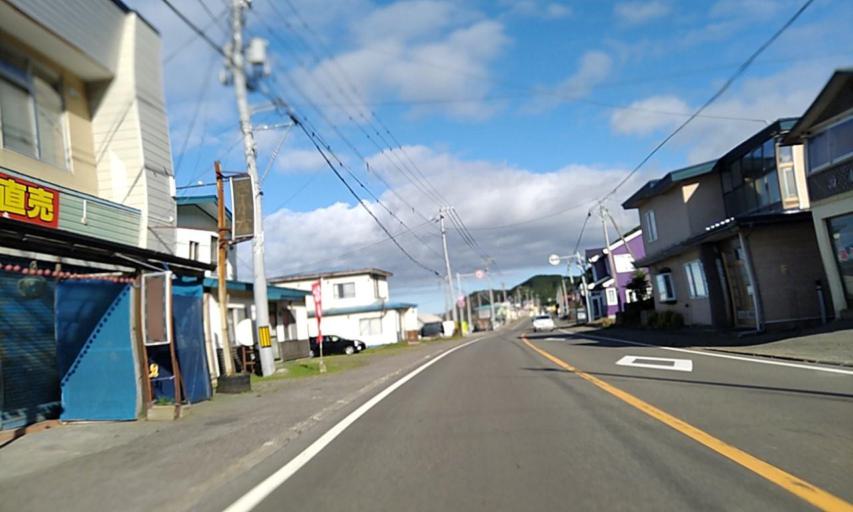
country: JP
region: Hokkaido
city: Shizunai-furukawacho
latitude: 42.1989
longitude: 142.6621
